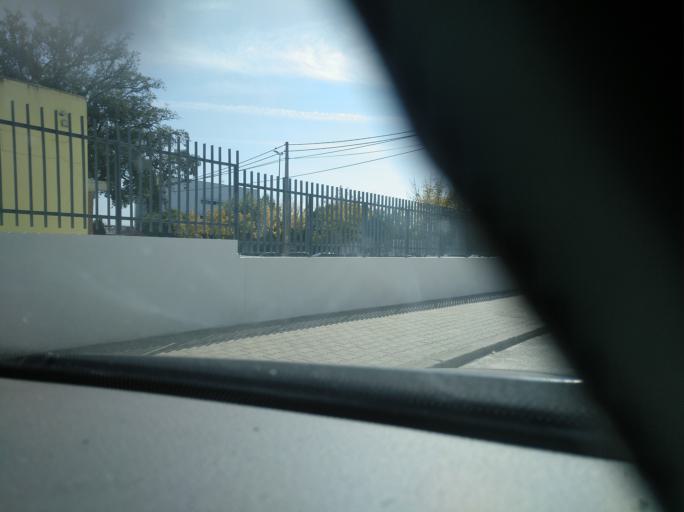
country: PT
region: Evora
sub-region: Vendas Novas
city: Vendas Novas
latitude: 38.6750
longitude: -8.4592
